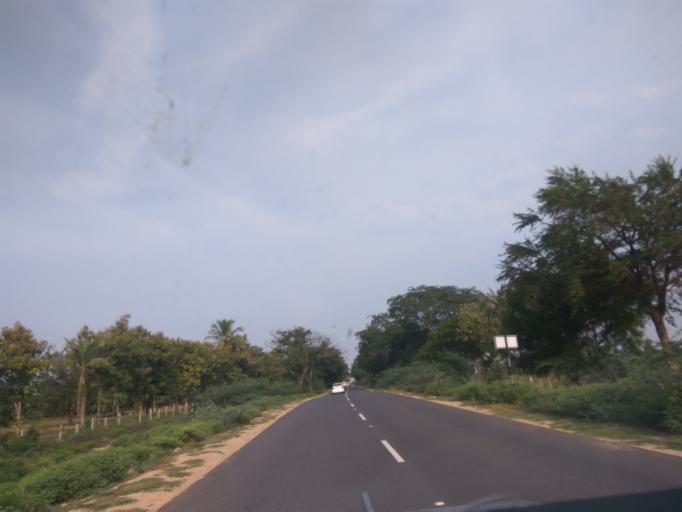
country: IN
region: Andhra Pradesh
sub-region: Guntur
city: Vinukonda
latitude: 16.0132
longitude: 79.6325
